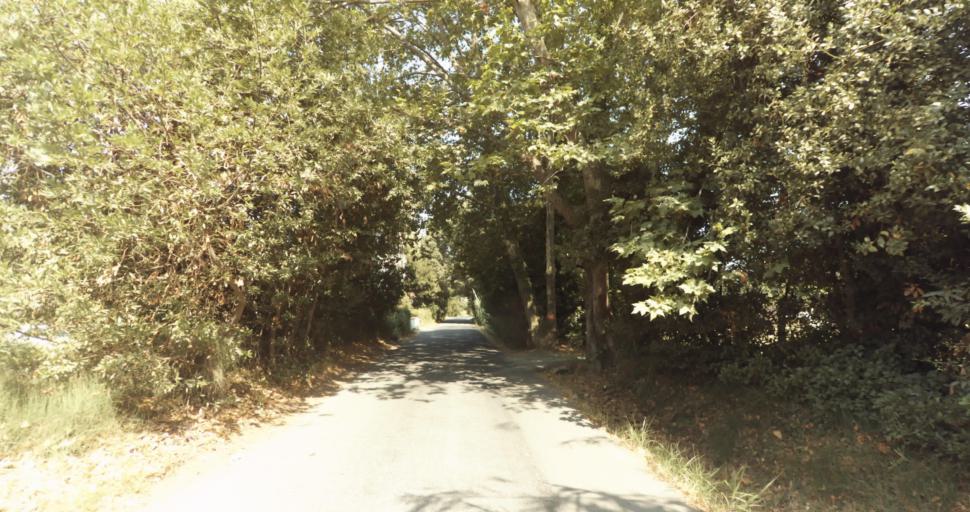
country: FR
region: Languedoc-Roussillon
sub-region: Departement des Pyrenees-Orientales
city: Latour-Bas-Elne
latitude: 42.6151
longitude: 2.9864
